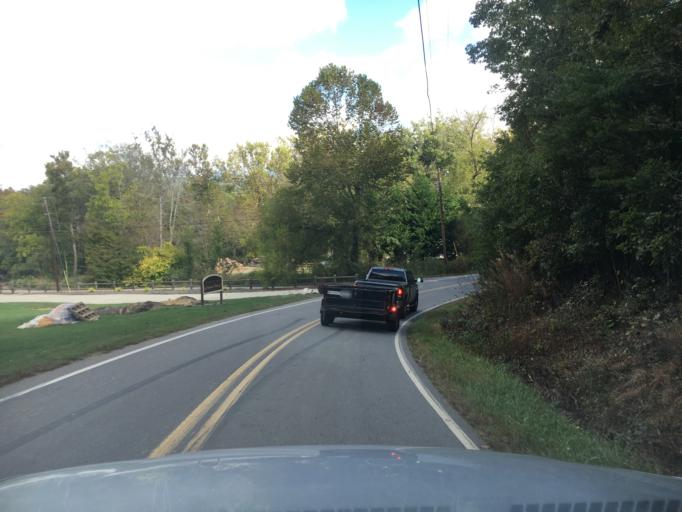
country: US
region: North Carolina
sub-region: Buncombe County
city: Swannanoa
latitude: 35.6037
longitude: -82.4327
